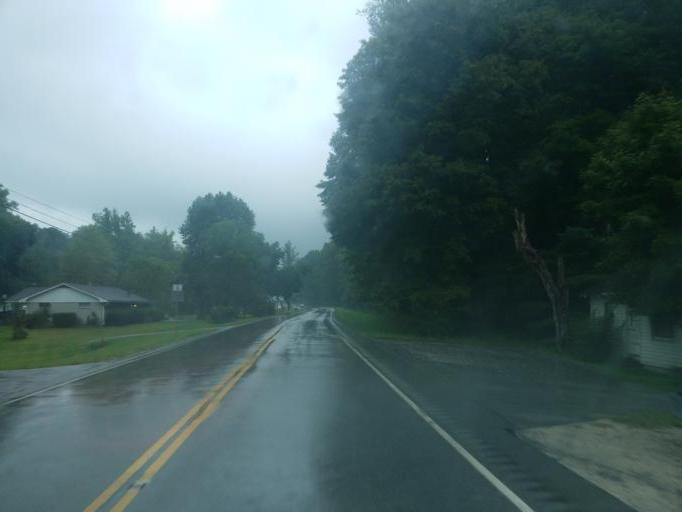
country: US
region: Kentucky
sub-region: Rowan County
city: Morehead
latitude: 38.2440
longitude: -83.3450
